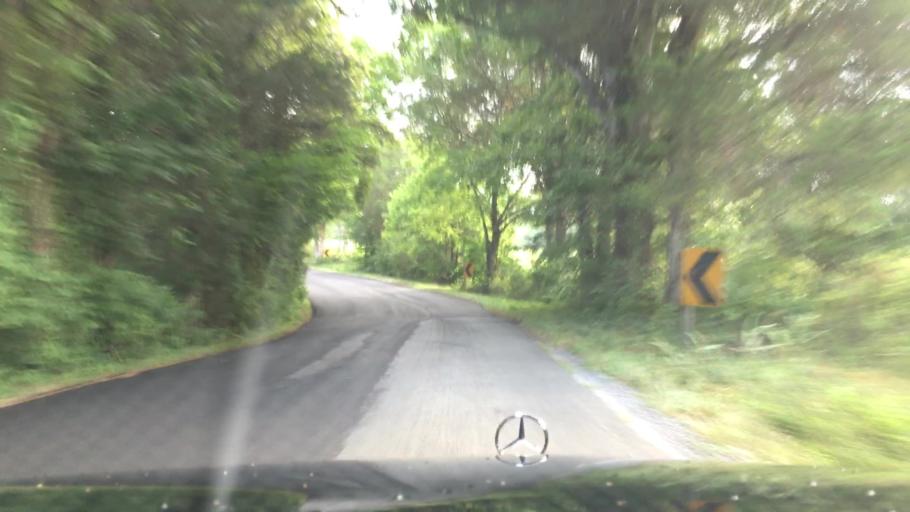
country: US
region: Virginia
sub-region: Campbell County
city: Timberlake
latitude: 37.2628
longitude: -79.3122
